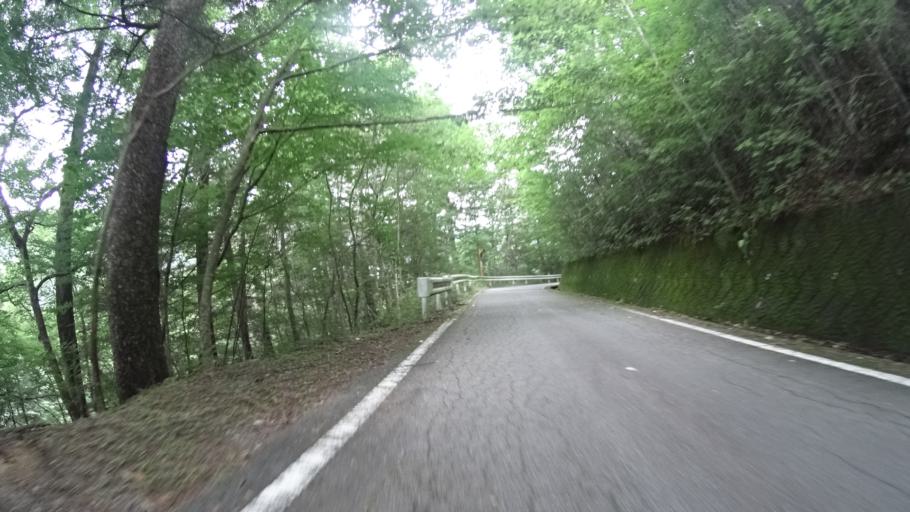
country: JP
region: Yamanashi
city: Kofu-shi
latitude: 35.8084
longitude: 138.6027
